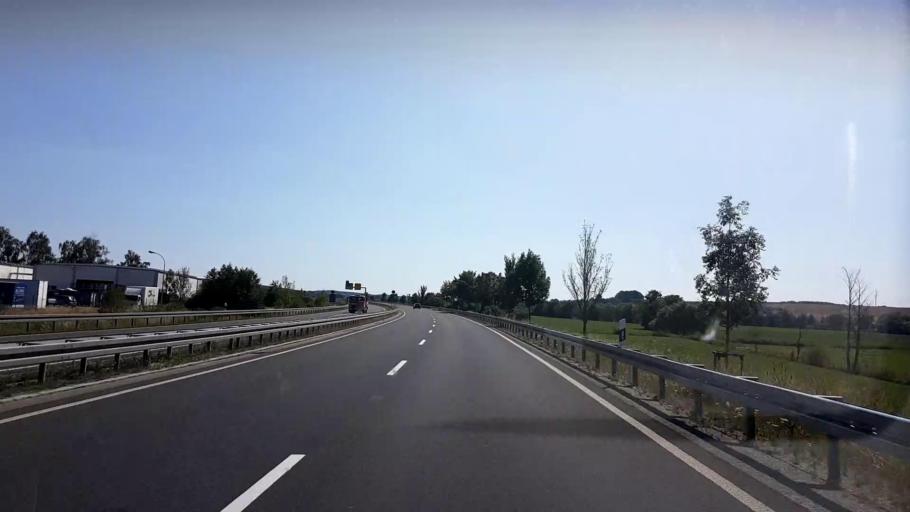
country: DE
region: Bavaria
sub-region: Upper Franconia
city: Grossheirath
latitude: 50.1959
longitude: 10.9579
